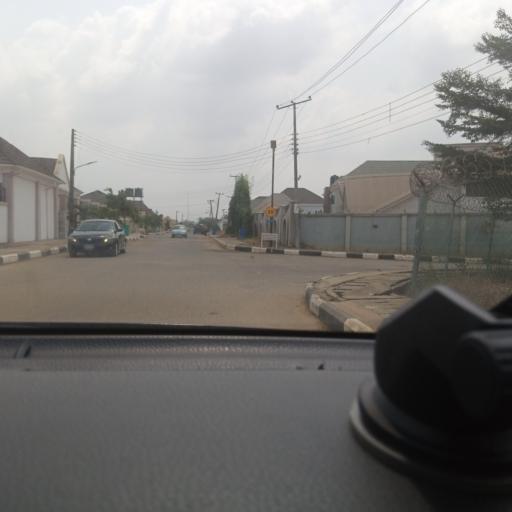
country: NG
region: Oyo
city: Ibadan
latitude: 7.4292
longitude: 3.9067
